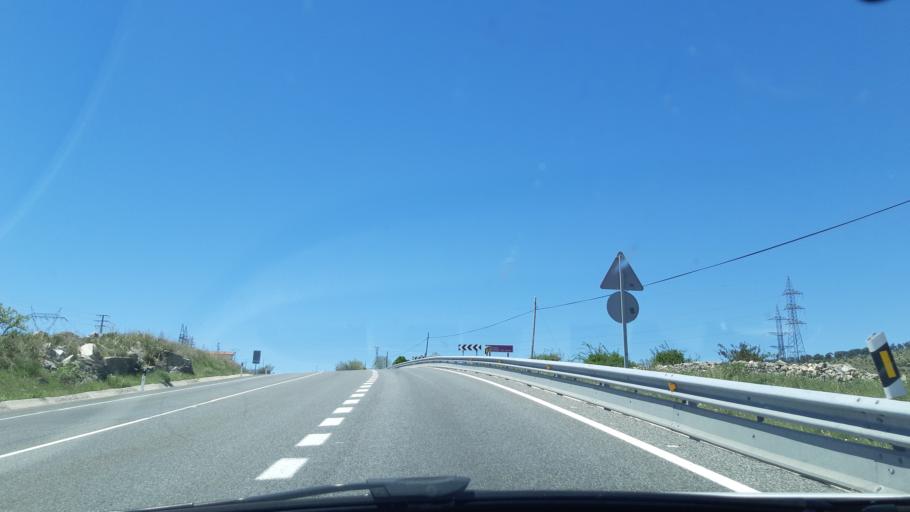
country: ES
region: Castille and Leon
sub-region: Provincia de Segovia
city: Vegas de Matute
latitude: 40.7423
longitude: -4.2665
